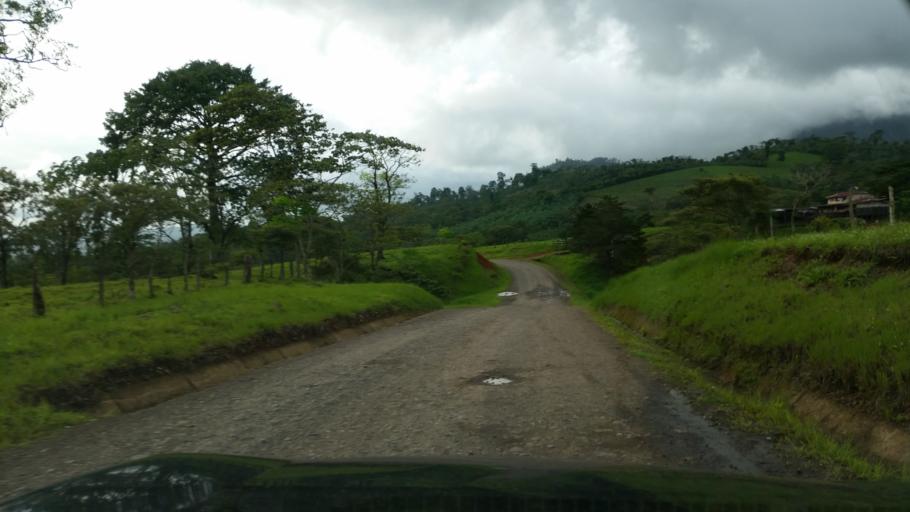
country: NI
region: Jinotega
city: Jinotega
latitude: 13.2689
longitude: -85.7312
